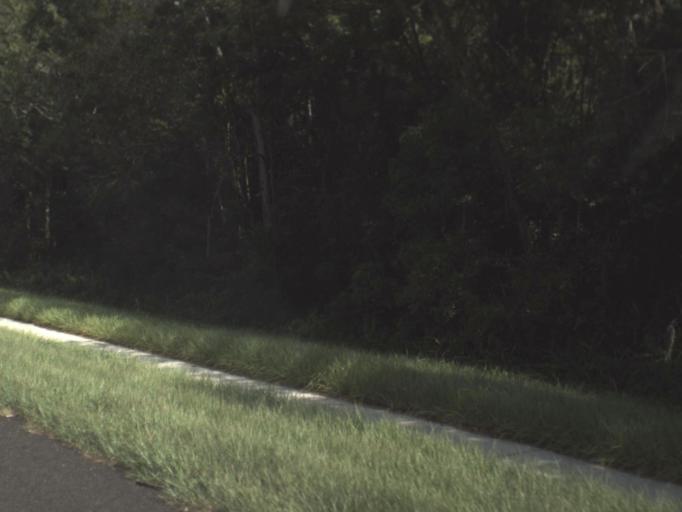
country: US
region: Florida
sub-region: Hillsborough County
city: Valrico
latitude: 27.9375
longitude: -82.1594
